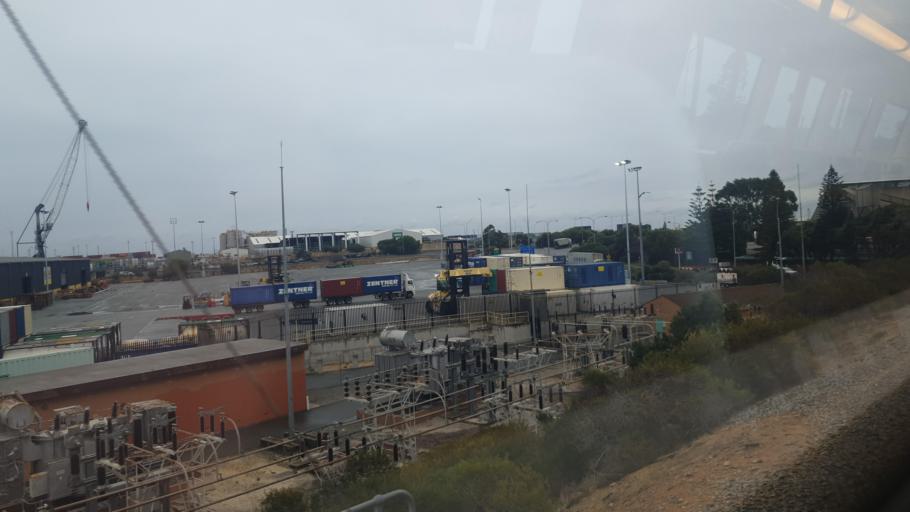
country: AU
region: Western Australia
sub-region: Fremantle
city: North Fremantle
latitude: -32.0379
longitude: 115.7529
